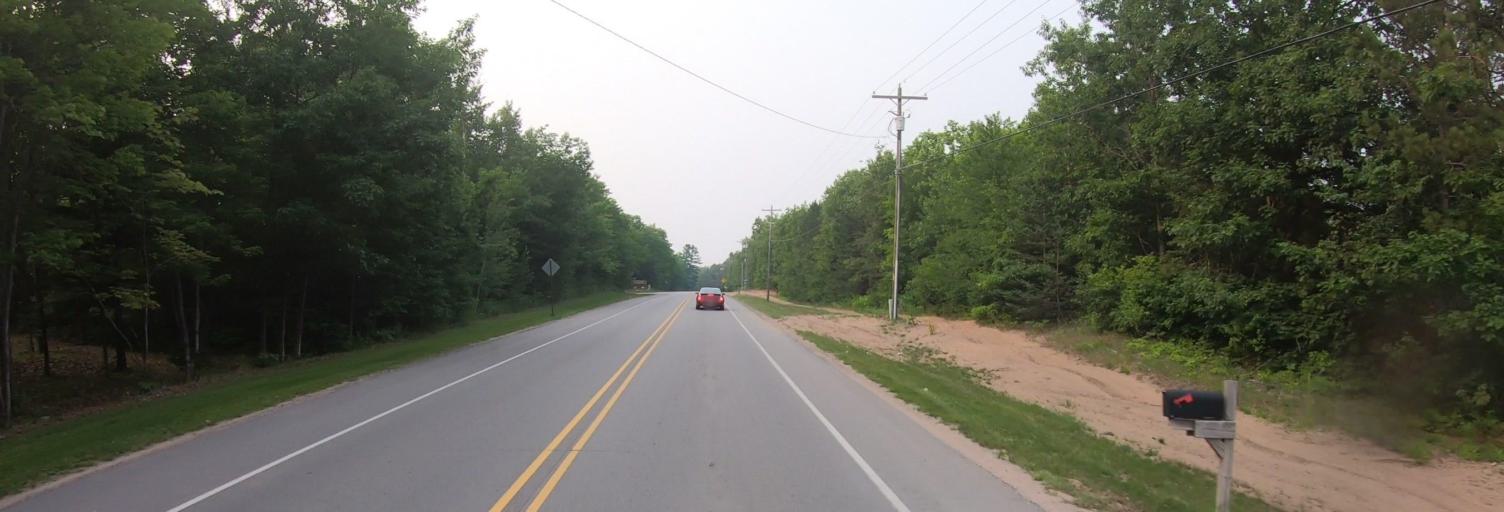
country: US
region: Michigan
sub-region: Chippewa County
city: Sault Ste. Marie
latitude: 46.4654
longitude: -84.6194
